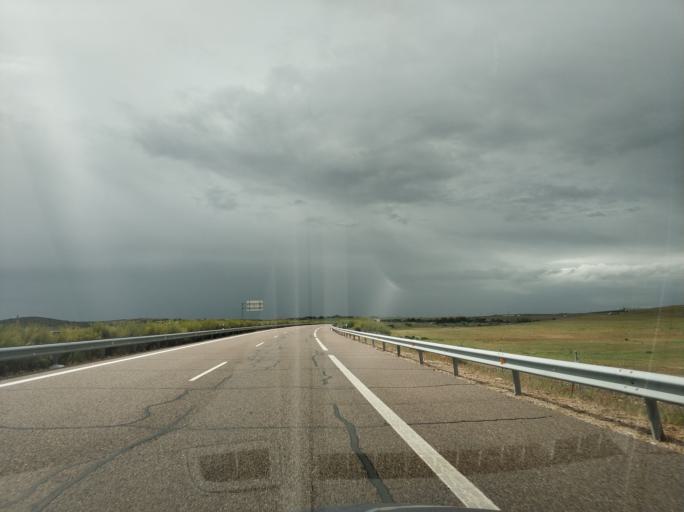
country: ES
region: Castille and Leon
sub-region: Provincia de Salamanca
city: Aldeatejada
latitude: 40.9257
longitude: -5.6733
